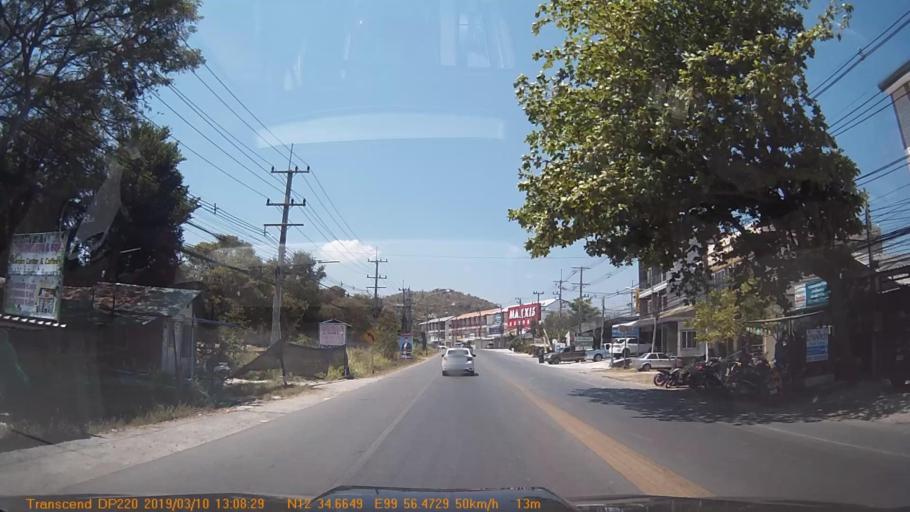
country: TH
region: Prachuap Khiri Khan
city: Hua Hin
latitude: 12.5778
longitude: 99.9412
